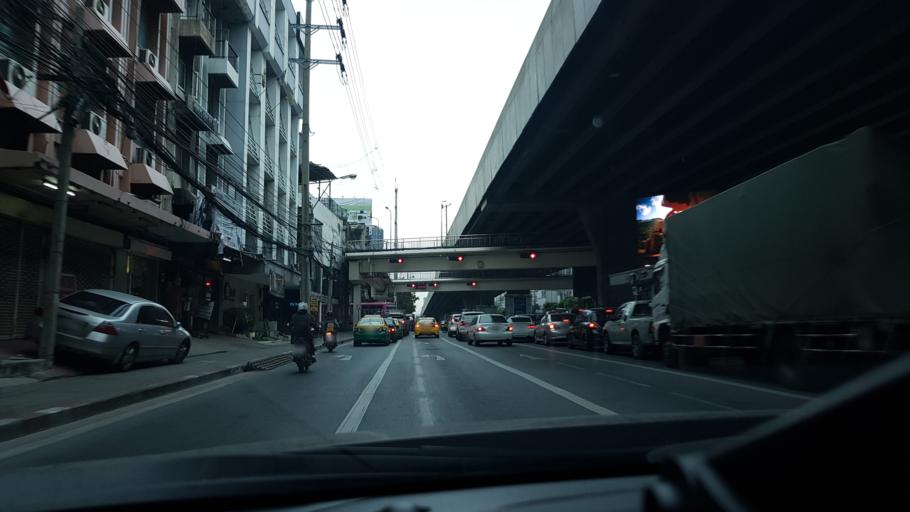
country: TH
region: Bangkok
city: Chatuchak
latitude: 13.8060
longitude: 100.5752
